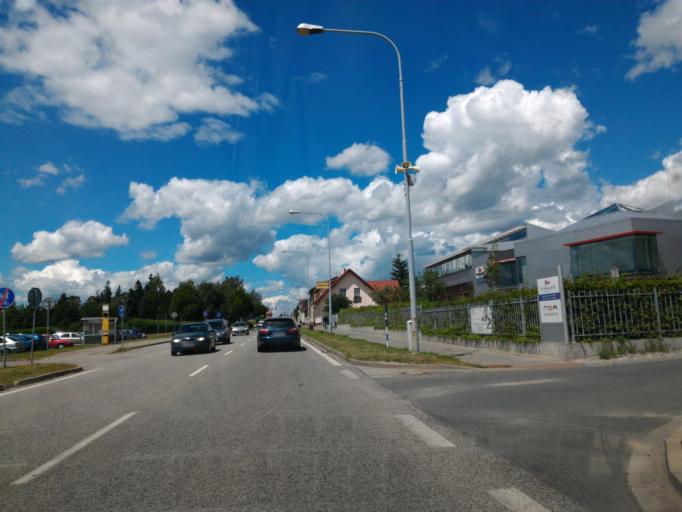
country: CZ
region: Vysocina
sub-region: Okres Zd'ar nad Sazavou
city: Zd'ar nad Sazavou
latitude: 49.5727
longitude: 15.9419
